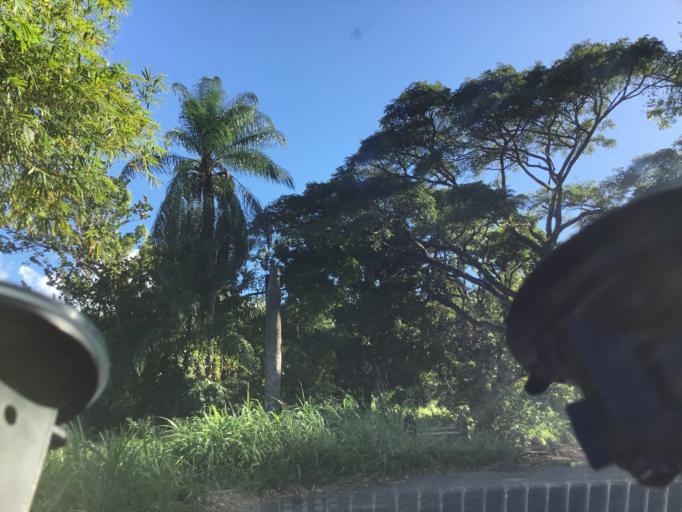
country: VC
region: Saint David
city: Chateaubelair
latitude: 13.3023
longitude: -61.2291
